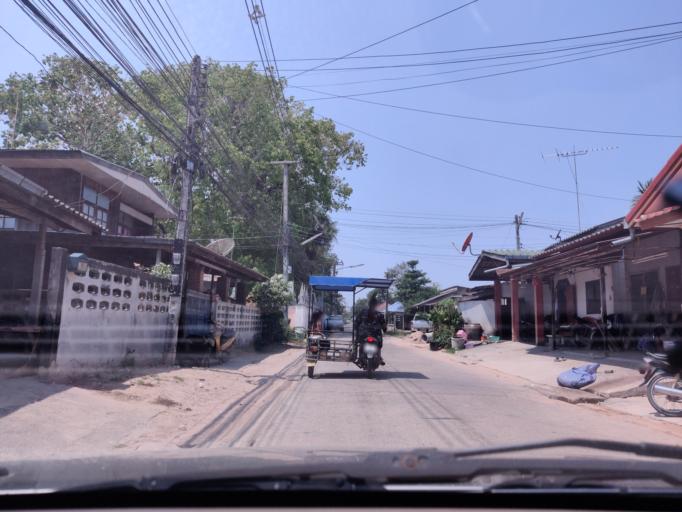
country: TH
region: Sisaket
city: Si Sa Ket
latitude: 15.1045
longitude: 104.3524
